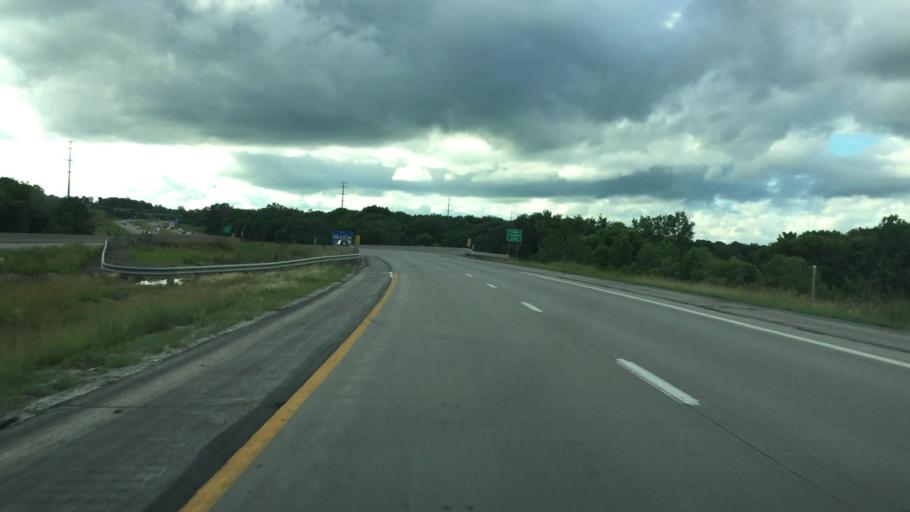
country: US
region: Iowa
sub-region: Polk County
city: Altoona
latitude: 41.6224
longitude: -93.4935
